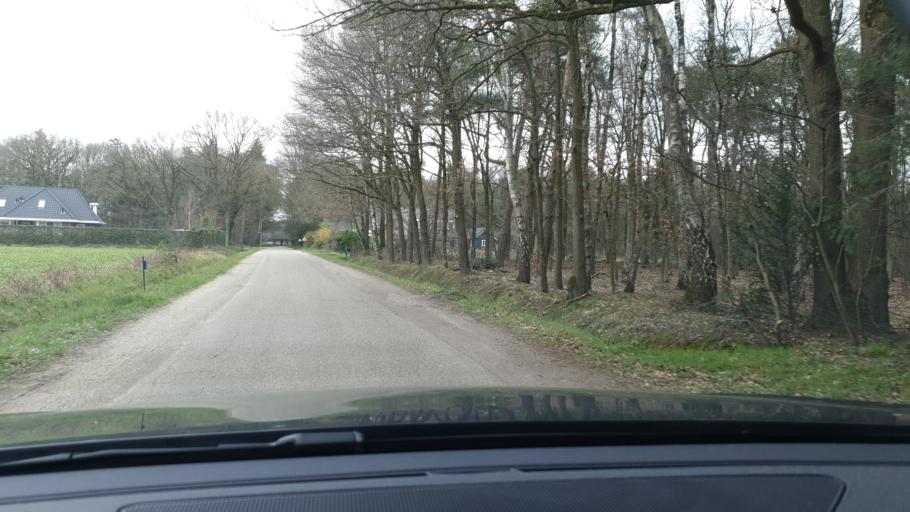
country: NL
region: North Brabant
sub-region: Gemeente Veldhoven
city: Oerle
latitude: 51.4227
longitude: 5.3487
